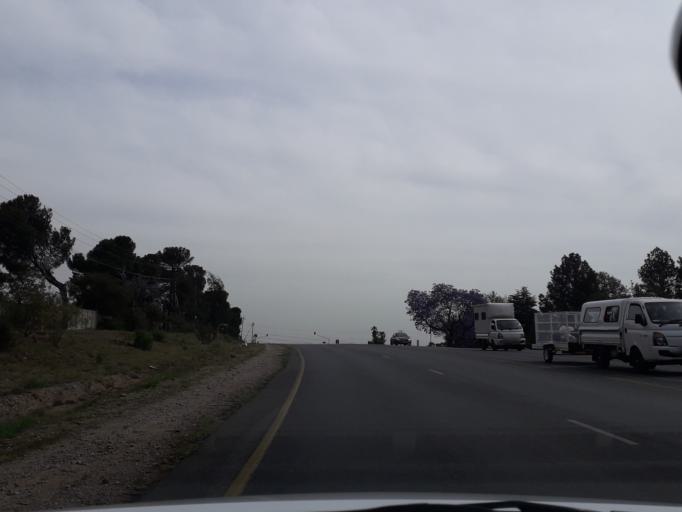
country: ZA
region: Gauteng
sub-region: City of Johannesburg Metropolitan Municipality
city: Diepsloot
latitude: -25.9886
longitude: 28.0528
